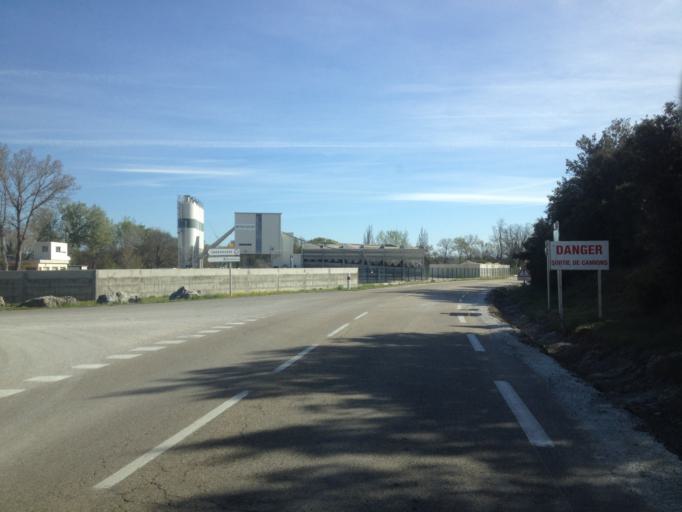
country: FR
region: Provence-Alpes-Cote d'Azur
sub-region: Departement du Vaucluse
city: Caderousse
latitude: 44.0880
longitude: 4.7819
